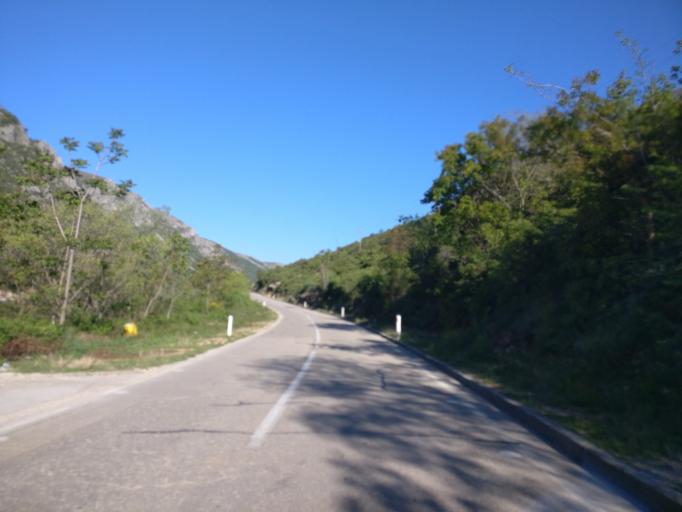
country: BA
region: Federation of Bosnia and Herzegovina
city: Stolac
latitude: 43.0754
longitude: 18.0281
